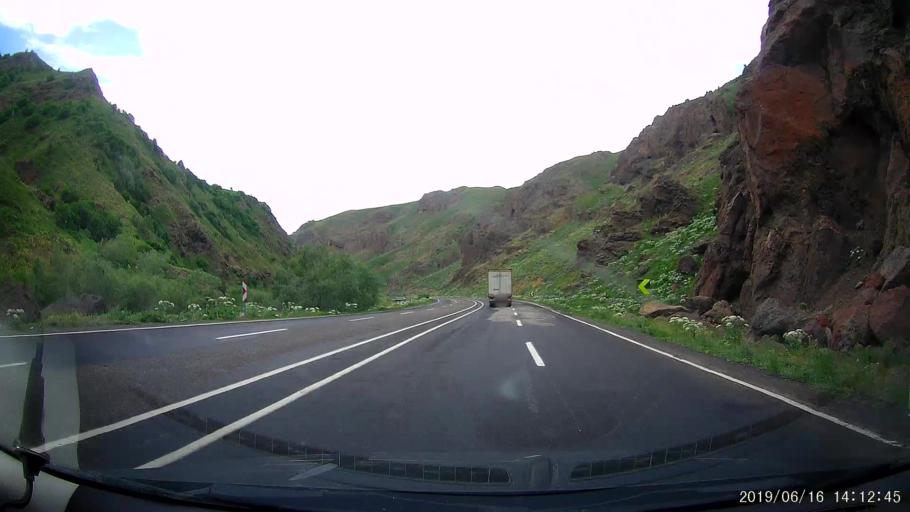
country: TR
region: Agri
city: Tahir
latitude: 39.7989
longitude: 42.5309
